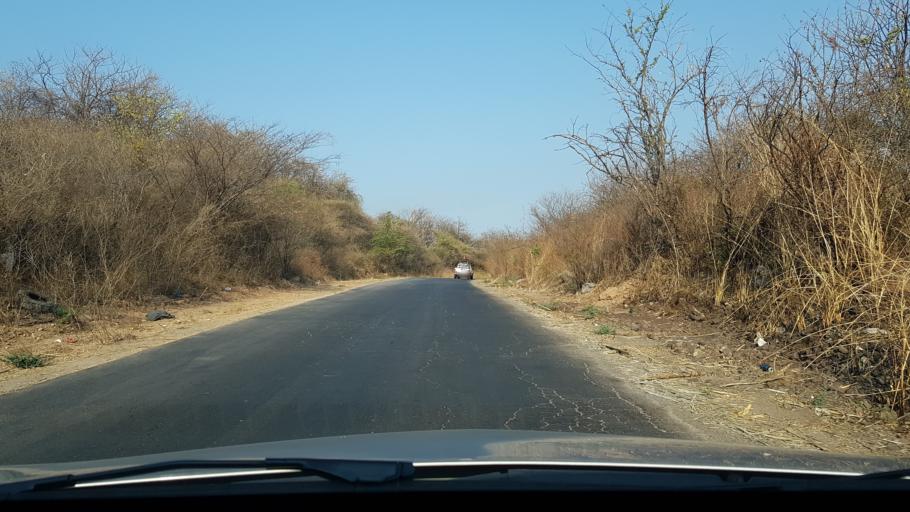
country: MX
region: Morelos
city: Tlaltizapan
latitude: 18.6759
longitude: -99.0753
